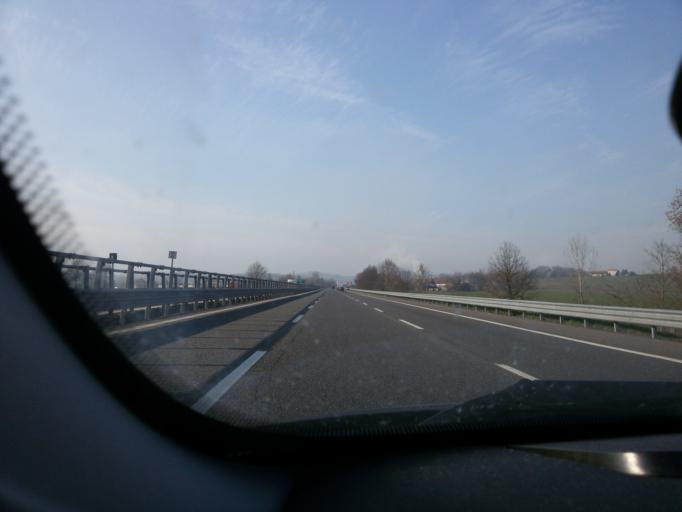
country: IT
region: Piedmont
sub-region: Provincia di Alessandria
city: Castelletto Monferrato
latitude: 44.9620
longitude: 8.5553
